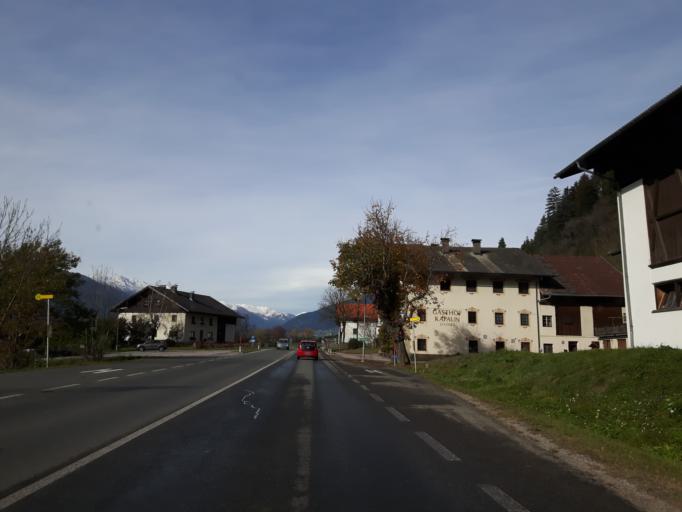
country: AT
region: Tyrol
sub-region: Politischer Bezirk Lienz
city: Lavant
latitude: 46.8080
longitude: 12.8564
